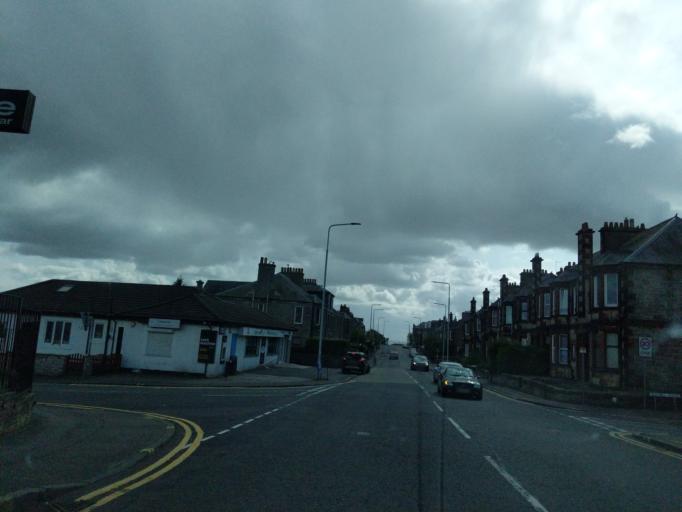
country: GB
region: Scotland
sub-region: Fife
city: Dunfermline
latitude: 56.0797
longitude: -3.4486
